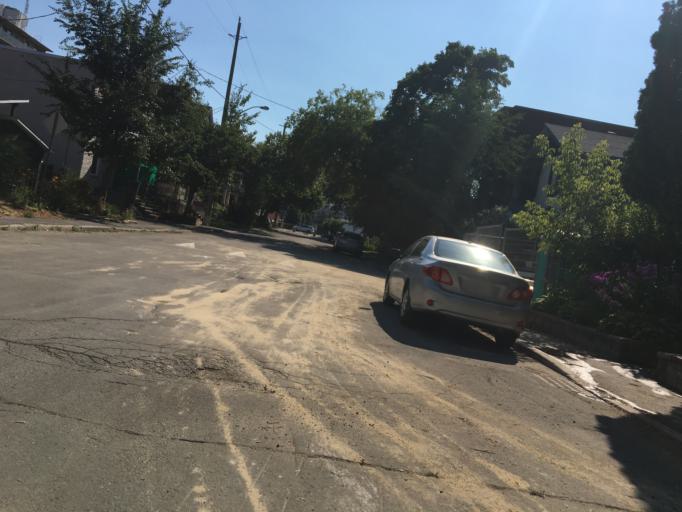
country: CA
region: Ontario
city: Ottawa
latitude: 45.4080
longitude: -75.7019
